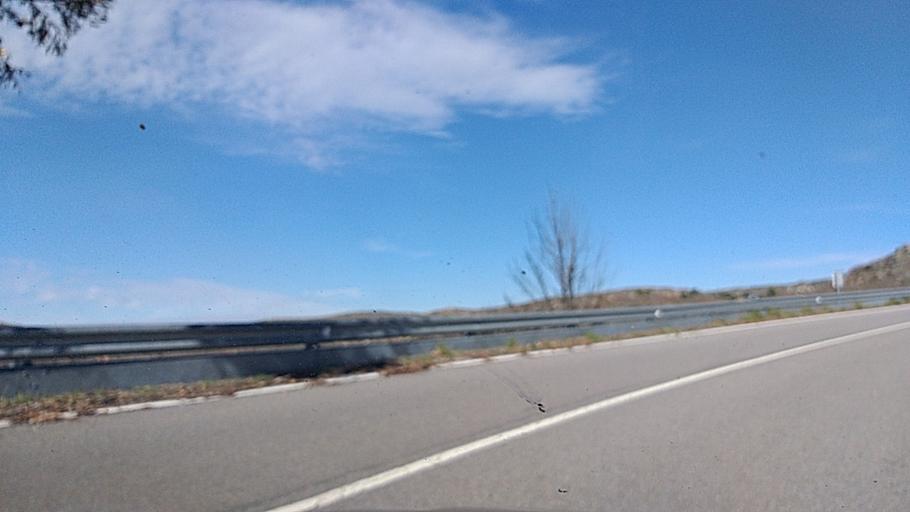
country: ES
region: Castille and Leon
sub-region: Provincia de Salamanca
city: Fuentes de Onoro
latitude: 40.6189
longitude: -6.9136
